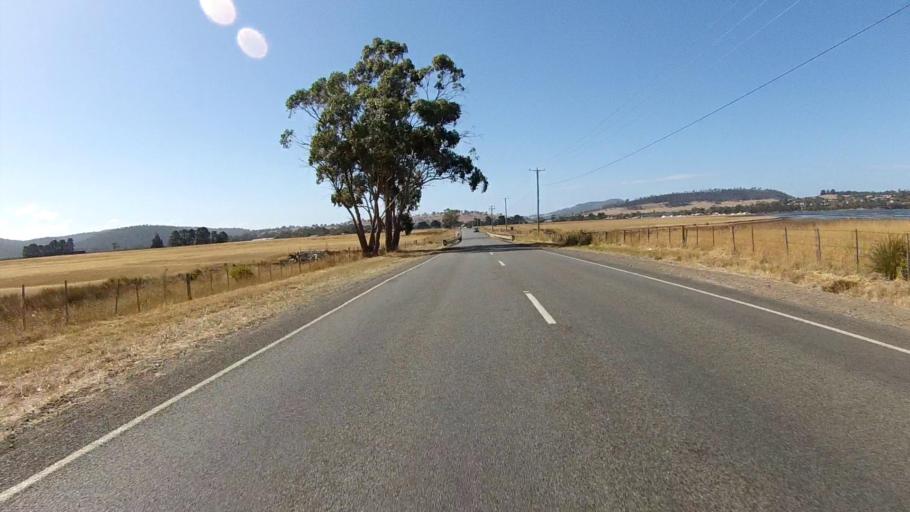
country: AU
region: Tasmania
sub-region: Sorell
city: Sorell
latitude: -42.5187
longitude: 147.9007
